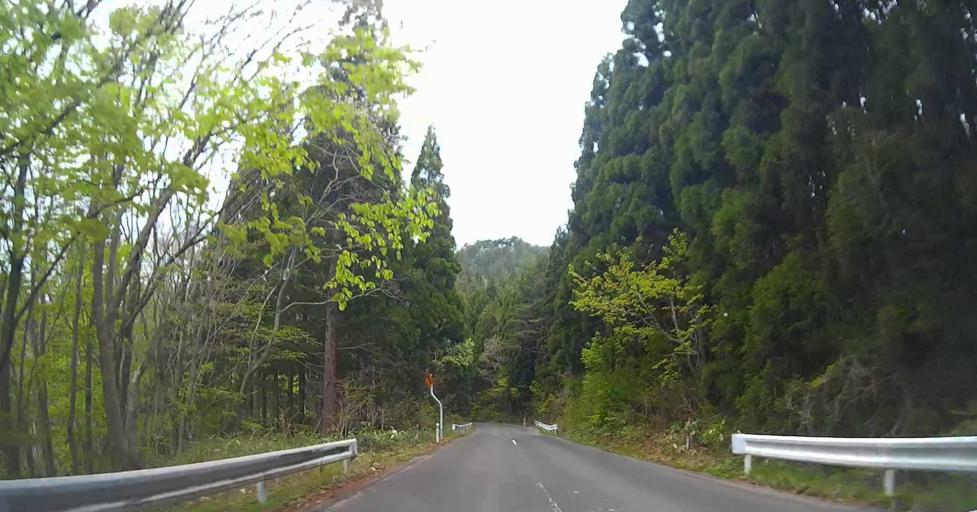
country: JP
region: Aomori
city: Goshogawara
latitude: 40.9049
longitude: 140.5130
